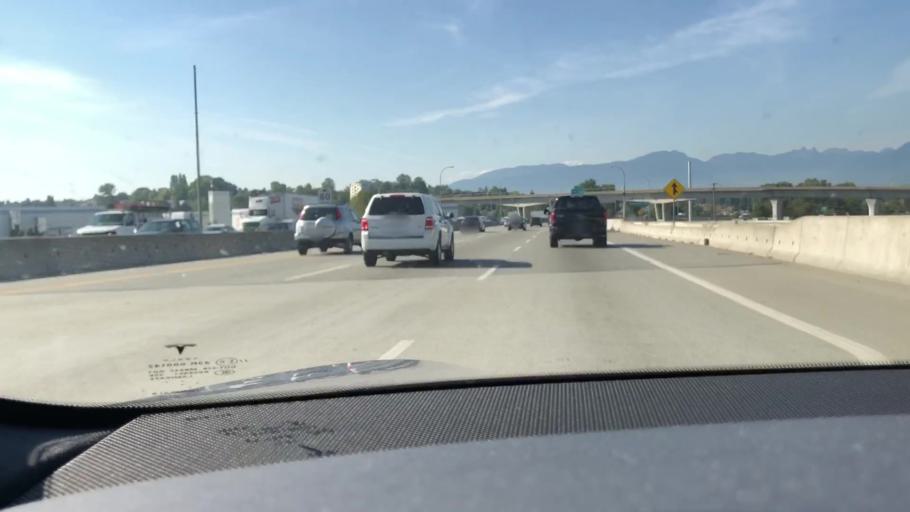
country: CA
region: British Columbia
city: Burnaby
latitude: 49.2606
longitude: -123.0229
